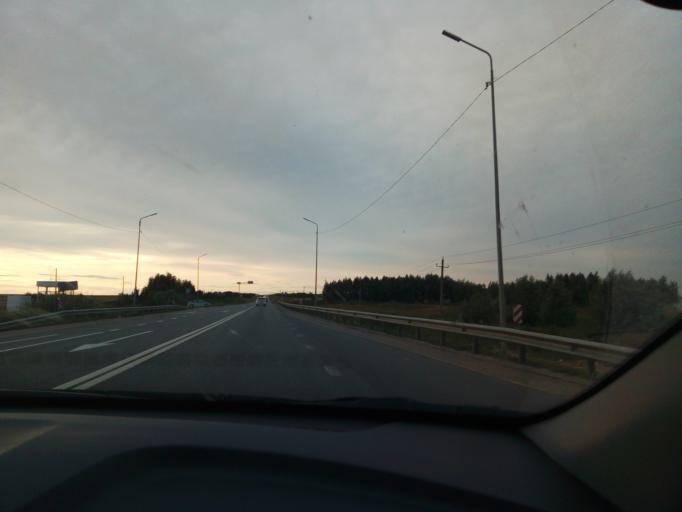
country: RU
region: Volgograd
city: Primorsk
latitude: 49.2667
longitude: 44.8792
